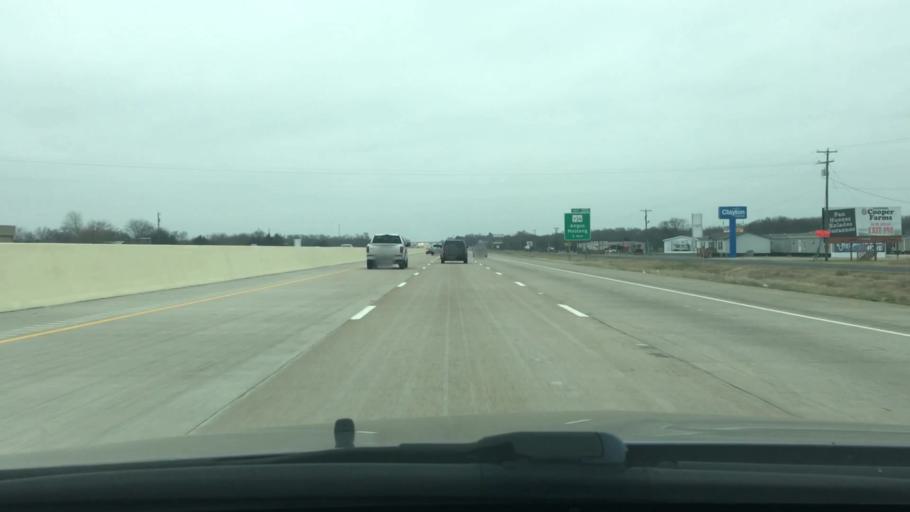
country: US
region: Texas
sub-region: Navarro County
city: Corsicana
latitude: 32.0257
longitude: -96.4410
